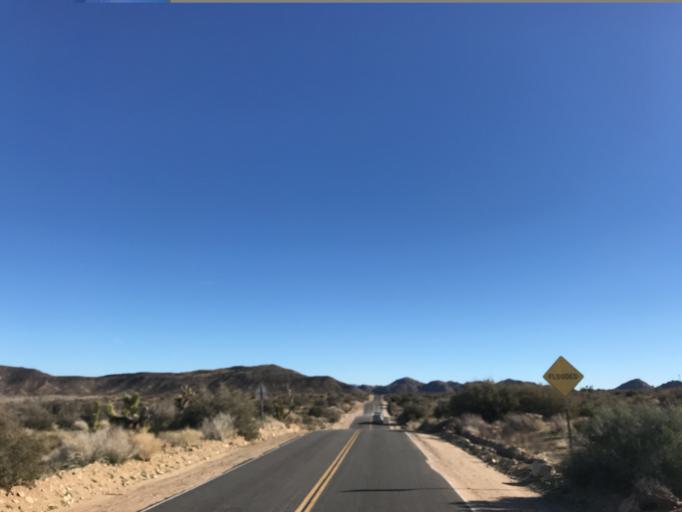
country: US
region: California
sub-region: San Bernardino County
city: Yucca Valley
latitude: 34.1812
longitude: -116.5354
